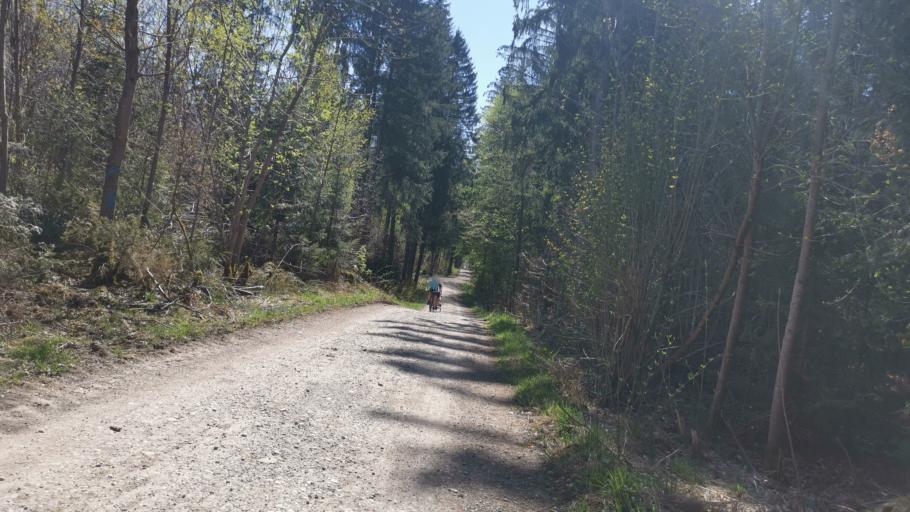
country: DE
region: Bavaria
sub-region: Upper Bavaria
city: Planegg
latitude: 48.0855
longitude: 11.4292
